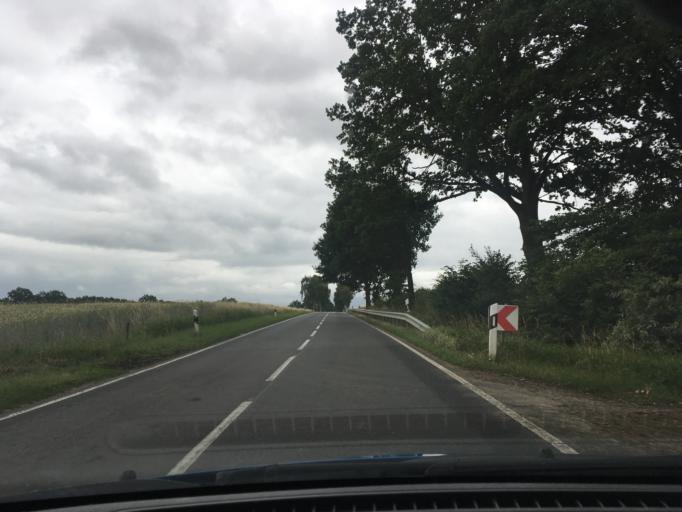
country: DE
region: Lower Saxony
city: Garlstorf
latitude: 53.2508
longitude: 10.0994
